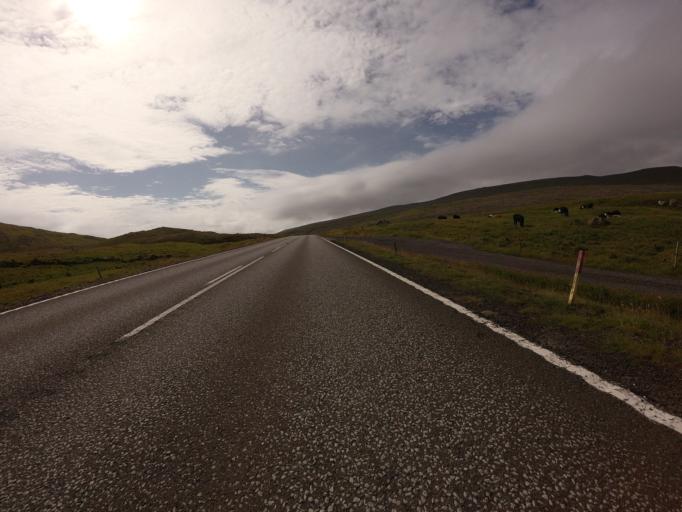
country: FO
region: Sandoy
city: Sandur
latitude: 61.8902
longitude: -6.8654
